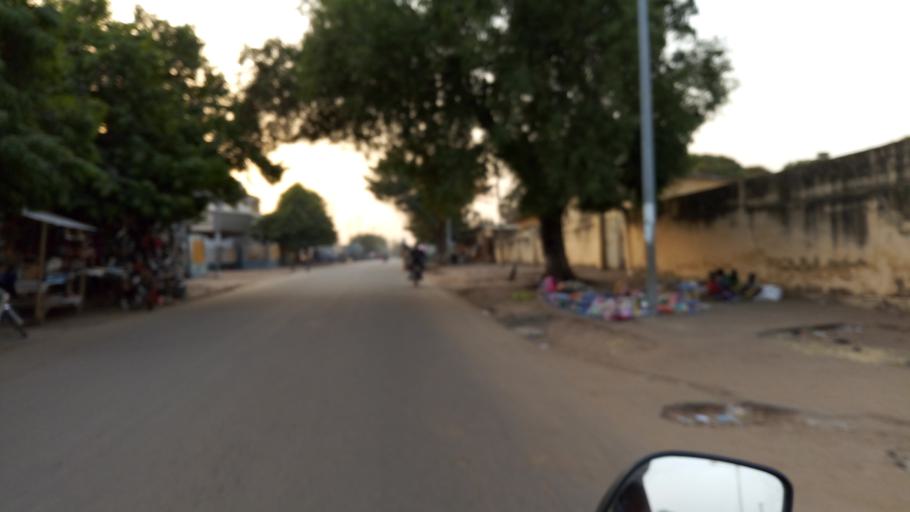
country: TG
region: Kara
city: Kara
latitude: 9.5486
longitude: 1.1955
